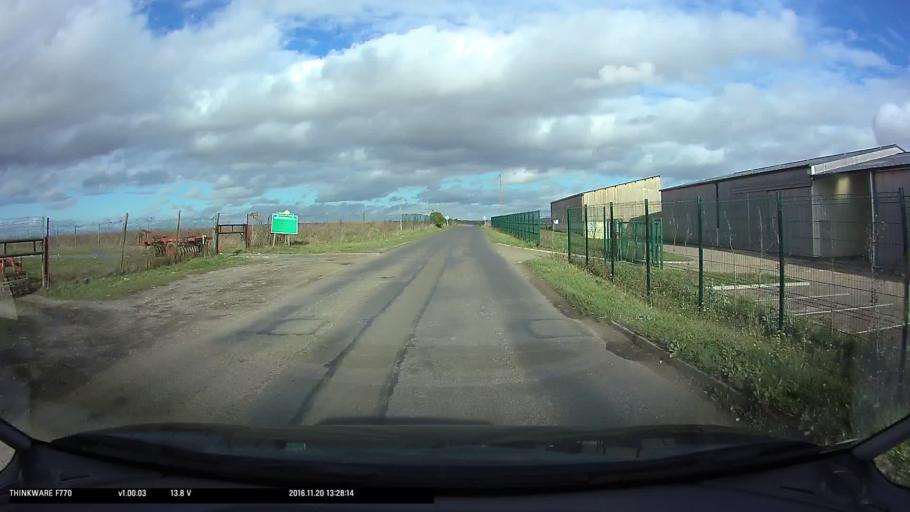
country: FR
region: Ile-de-France
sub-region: Departement du Val-d'Oise
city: Courdimanche
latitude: 49.0622
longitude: 2.0018
